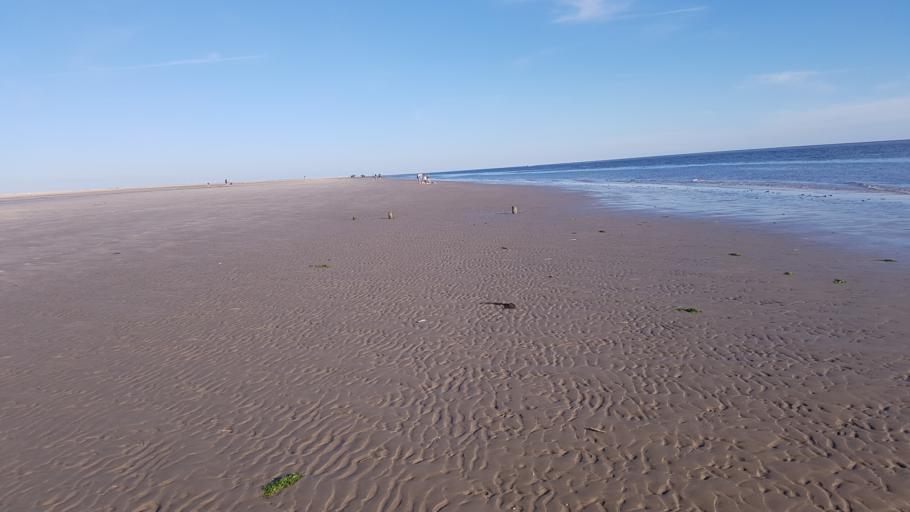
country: DE
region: Schleswig-Holstein
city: List
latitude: 55.0740
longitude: 8.4864
